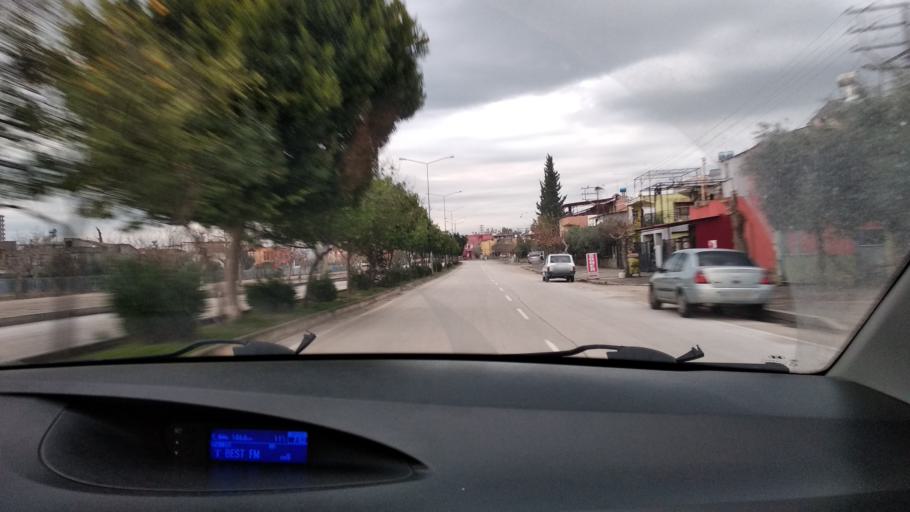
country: TR
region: Adana
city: Yuregir
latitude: 37.0126
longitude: 35.3875
